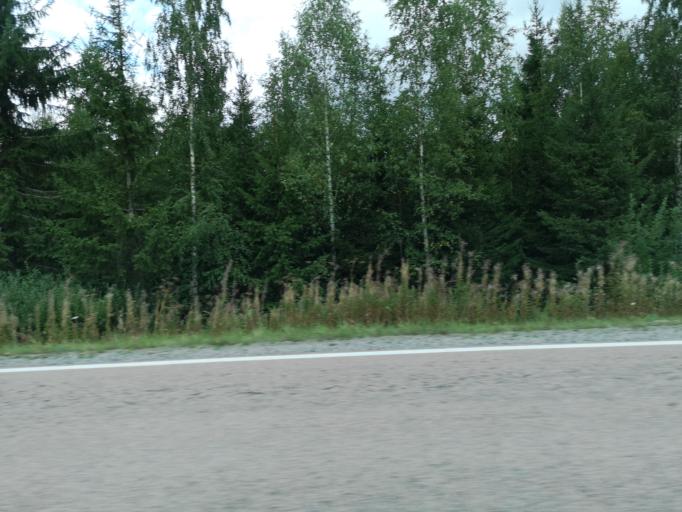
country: FI
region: Central Finland
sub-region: Jyvaeskylae
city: Hankasalmi
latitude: 62.3580
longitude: 26.5626
